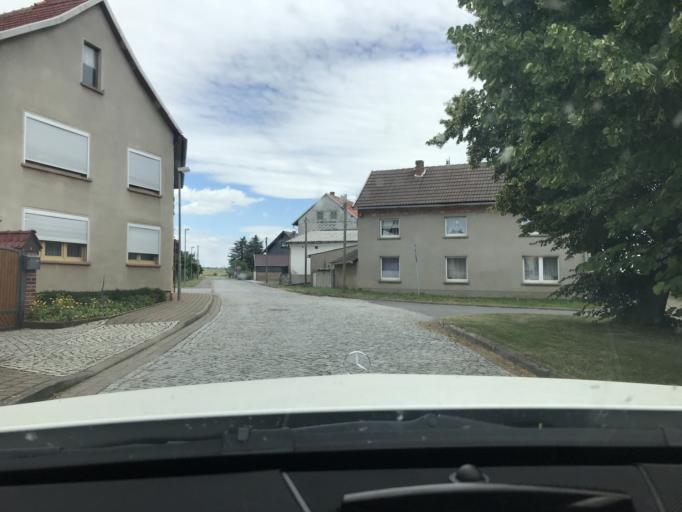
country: DE
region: Thuringia
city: Holzsussra
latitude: 51.2930
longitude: 10.6980
